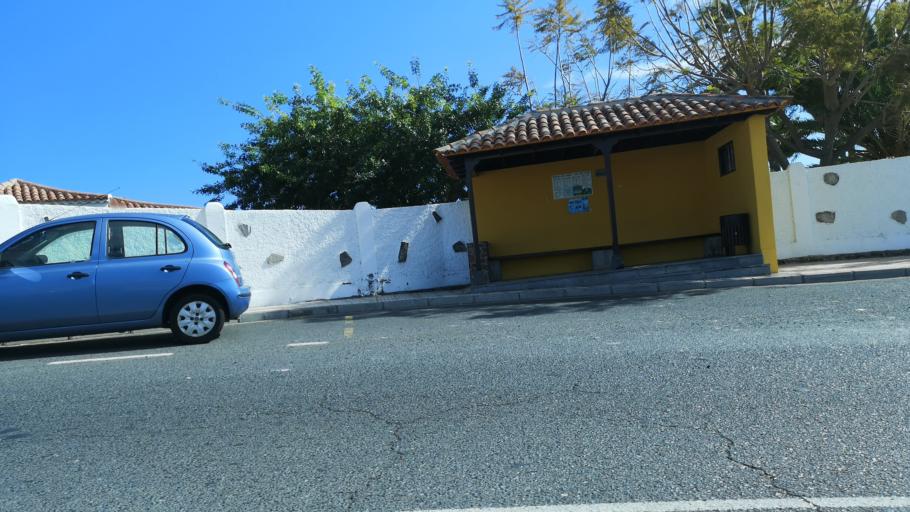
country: ES
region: Canary Islands
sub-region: Provincia de Santa Cruz de Tenerife
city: Alajero
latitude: 28.0308
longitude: -17.1903
